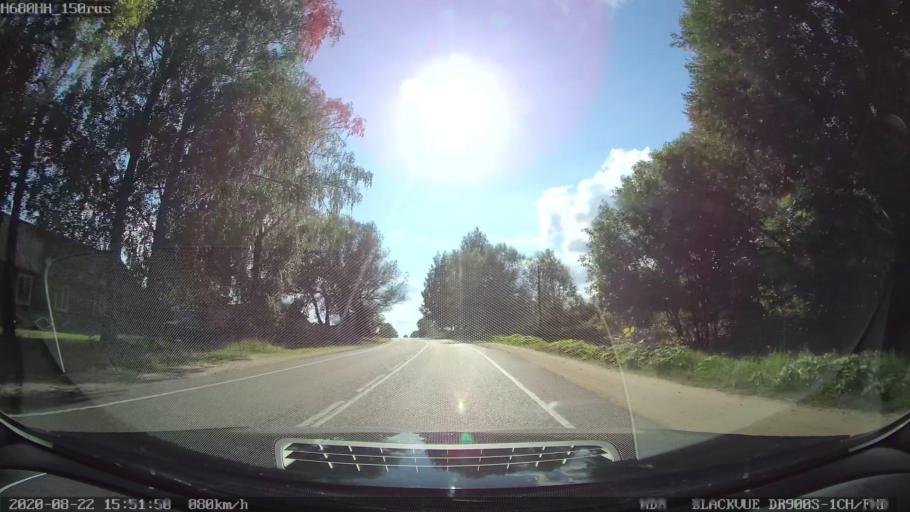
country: RU
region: Tverskaya
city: Bezhetsk
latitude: 57.6618
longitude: 36.4164
